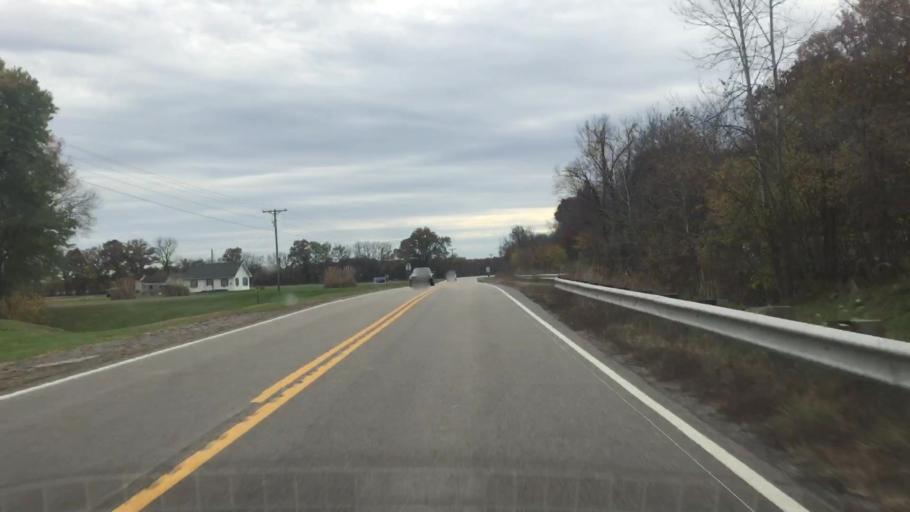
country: US
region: Missouri
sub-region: Callaway County
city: Holts Summit
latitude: 38.6036
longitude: -91.9936
